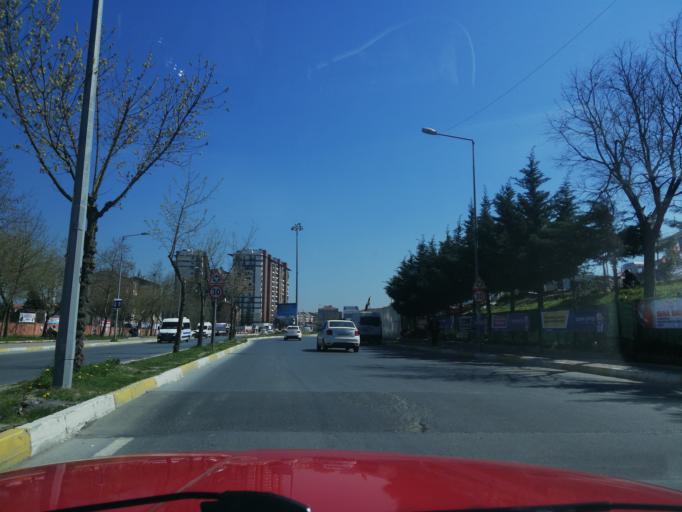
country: TR
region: Istanbul
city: Sisli
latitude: 41.0801
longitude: 28.9342
